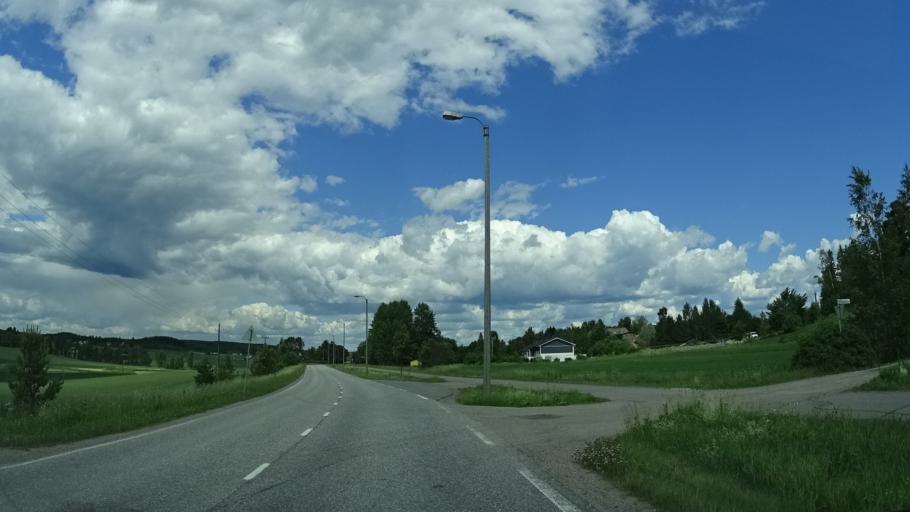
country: FI
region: Uusimaa
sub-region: Helsinki
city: Nurmijaervi
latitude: 60.3969
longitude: 24.6400
